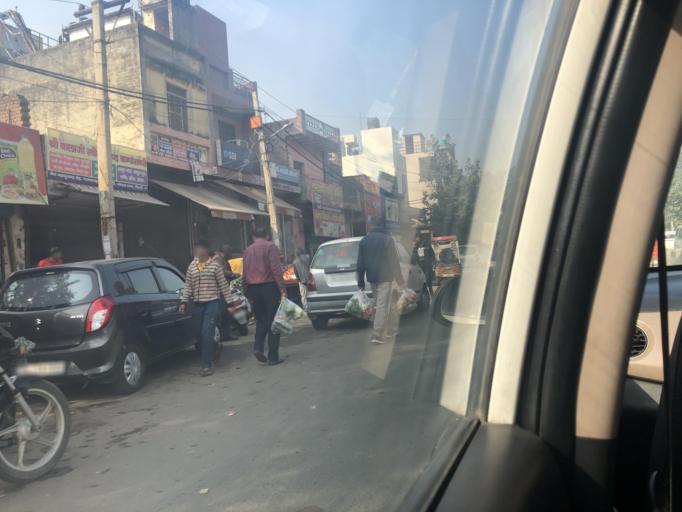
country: IN
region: Haryana
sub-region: Jhajjar
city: Bahadurgarh
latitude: 28.6144
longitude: 76.9783
